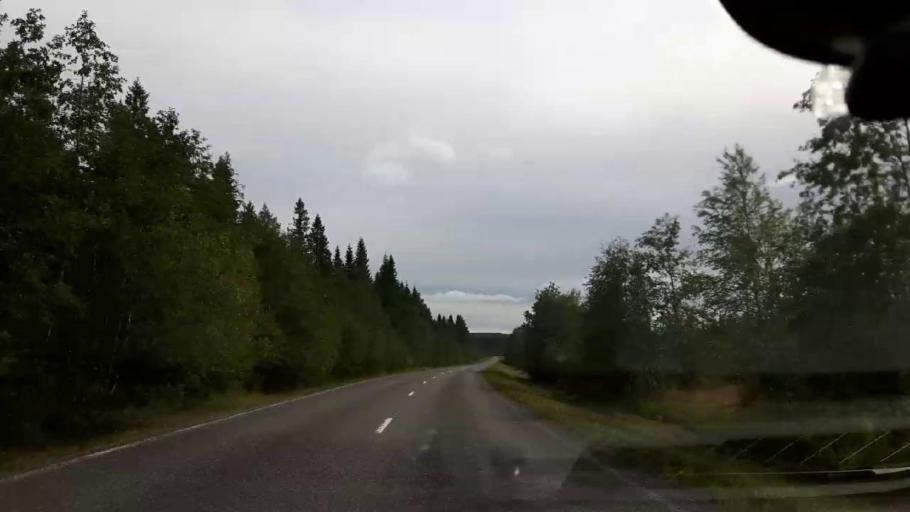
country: SE
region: Jaemtland
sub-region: Ragunda Kommun
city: Hammarstrand
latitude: 63.1324
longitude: 15.8814
